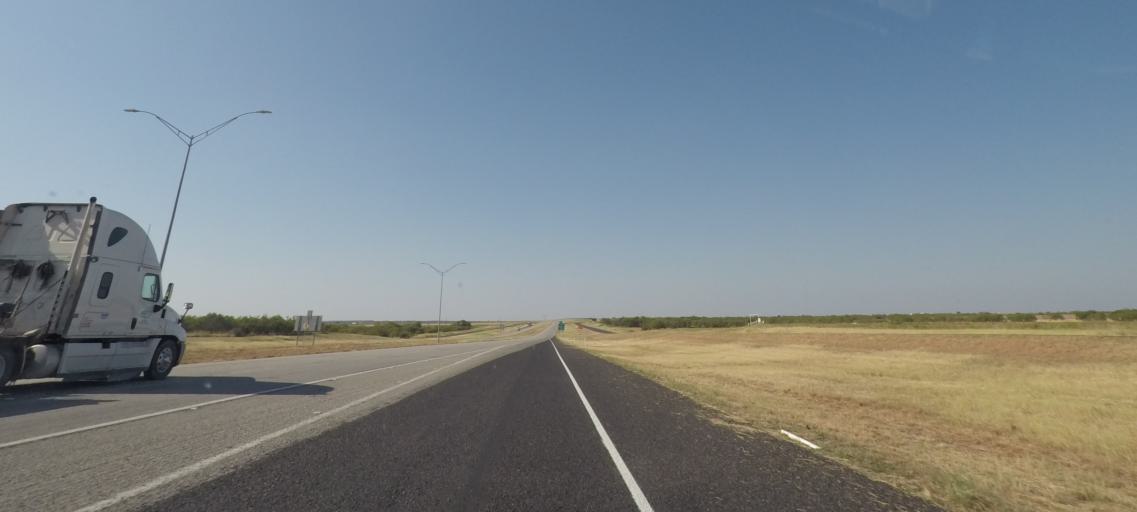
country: US
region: Texas
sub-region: Baylor County
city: Seymour
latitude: 33.6018
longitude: -99.2417
